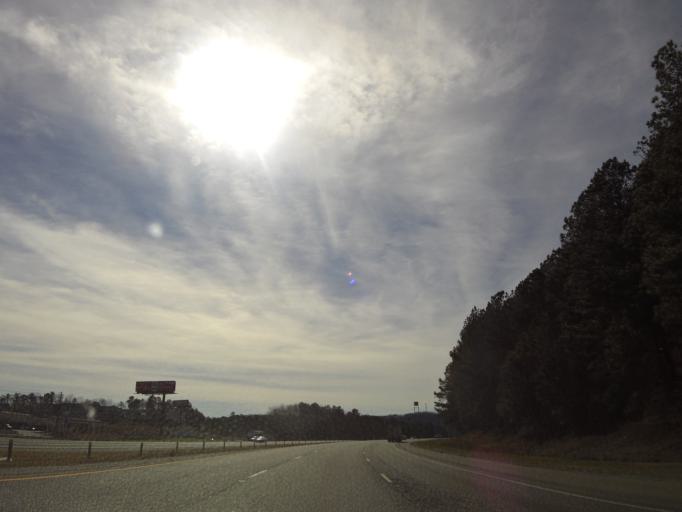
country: US
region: Georgia
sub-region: Bartow County
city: Cartersville
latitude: 34.2169
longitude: -84.7534
